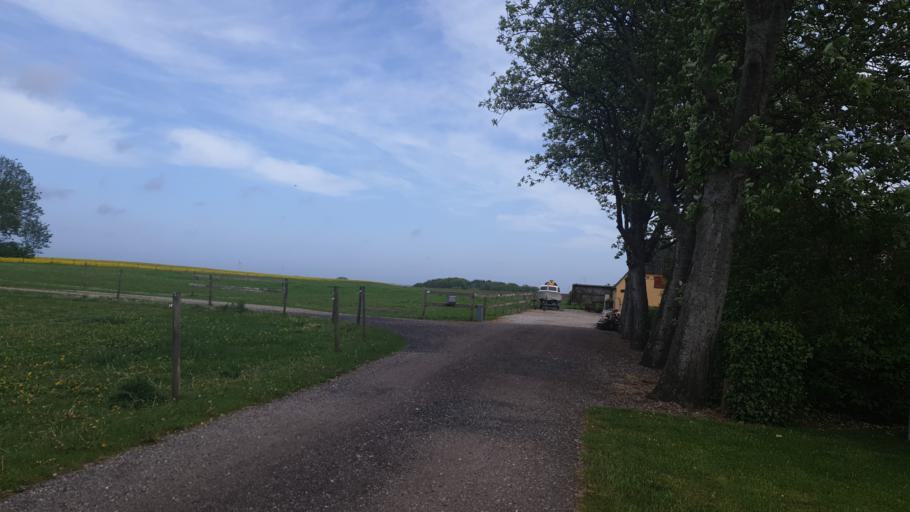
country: DK
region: Central Jutland
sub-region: Hedensted Kommune
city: Hedensted
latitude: 55.8137
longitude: 9.6974
